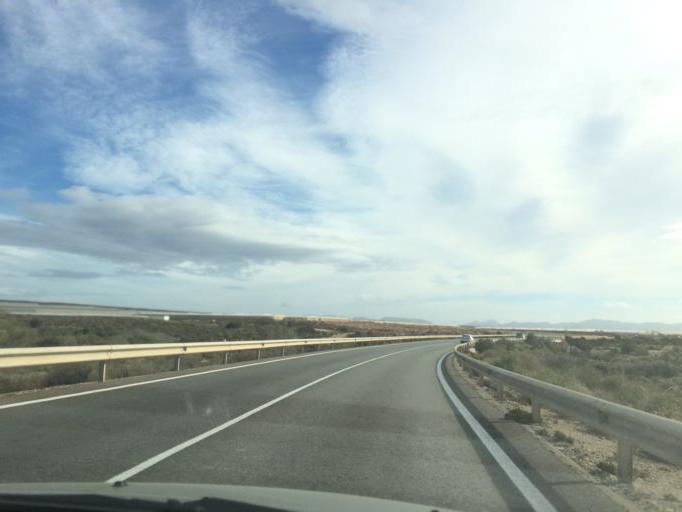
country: ES
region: Andalusia
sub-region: Provincia de Almeria
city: Retamar
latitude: 36.8432
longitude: -2.2998
